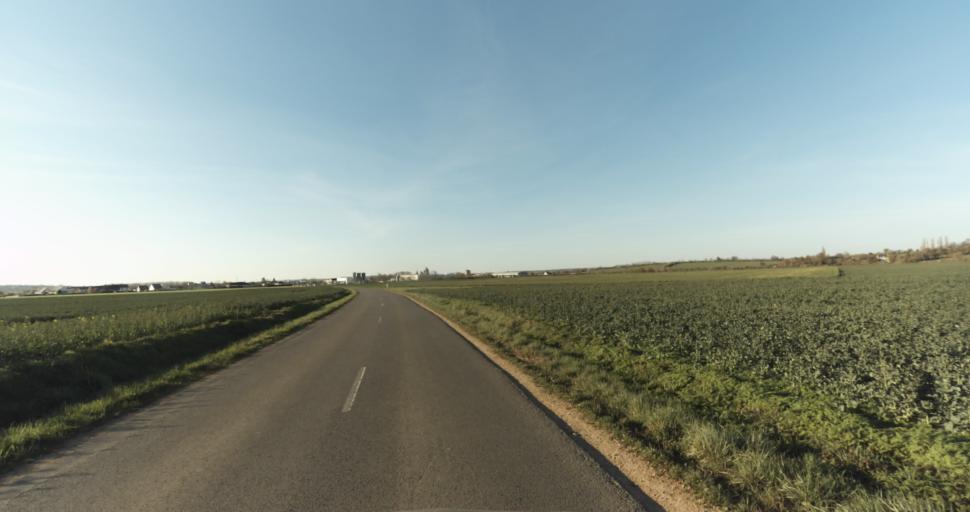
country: FR
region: Lower Normandy
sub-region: Departement du Calvados
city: Saint-Pierre-sur-Dives
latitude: 49.0080
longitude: -0.0261
